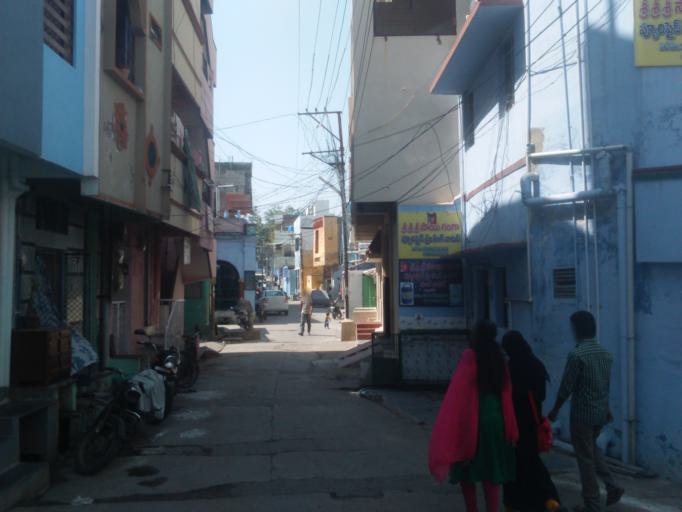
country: IN
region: Telangana
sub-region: Mahbubnagar
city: Alampur
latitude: 15.8223
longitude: 78.0418
